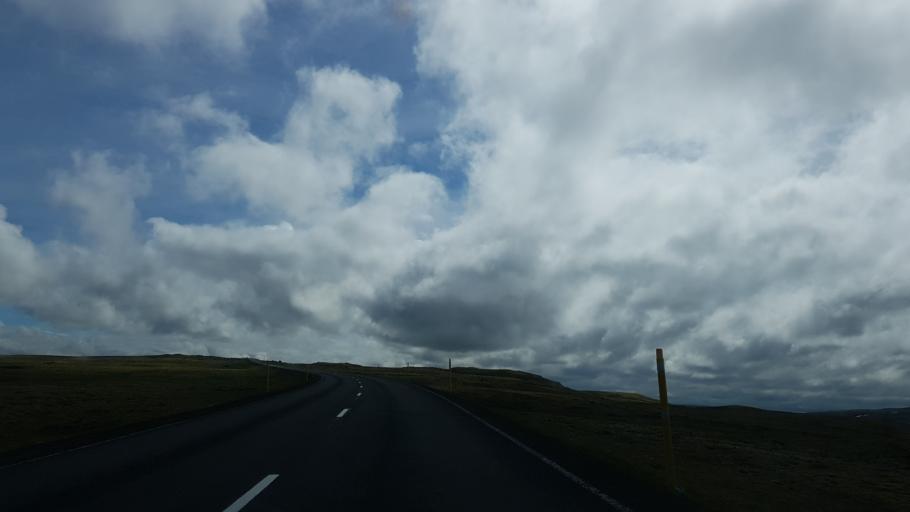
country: IS
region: West
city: Borgarnes
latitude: 64.9984
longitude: -21.0684
